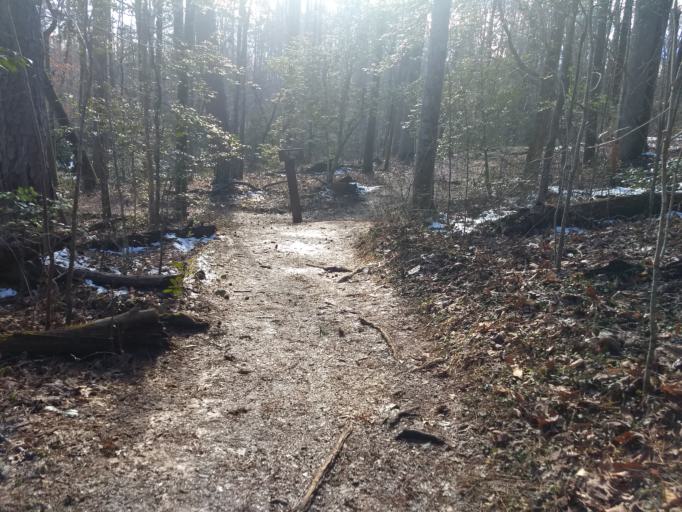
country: US
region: South Carolina
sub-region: Greenville County
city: Wade Hampton
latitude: 34.9283
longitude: -82.3757
